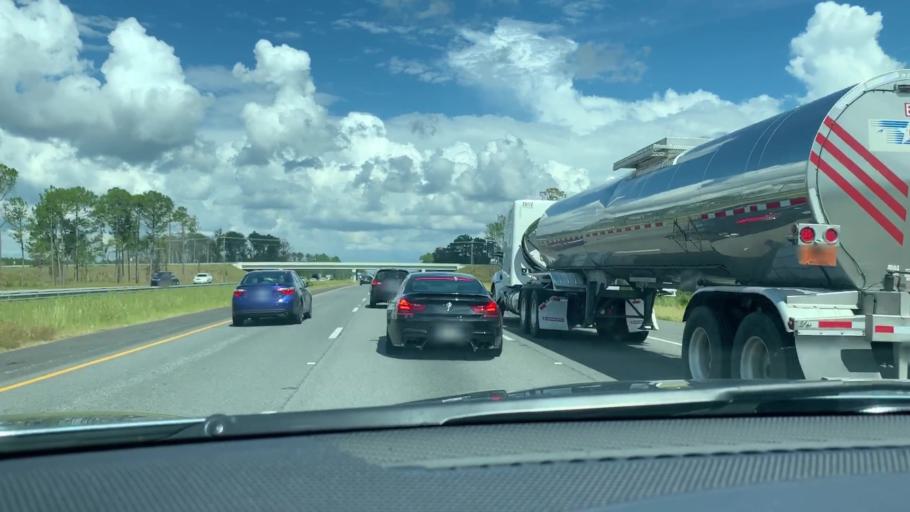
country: US
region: Georgia
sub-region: Camden County
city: Woodbine
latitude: 31.0543
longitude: -81.6416
